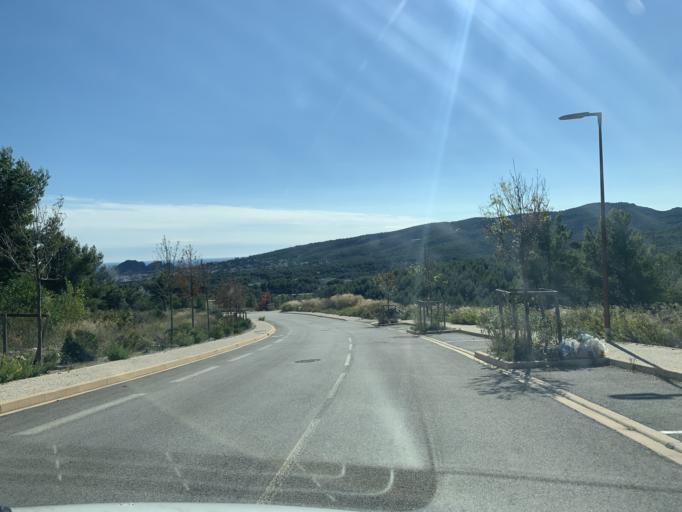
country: FR
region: Provence-Alpes-Cote d'Azur
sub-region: Departement des Bouches-du-Rhone
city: La Ciotat
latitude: 43.2090
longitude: 5.5933
